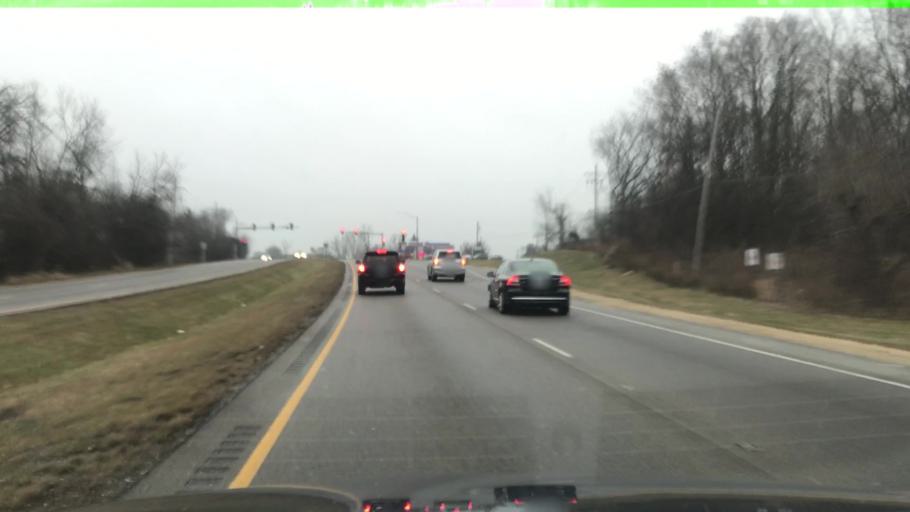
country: US
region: Illinois
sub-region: Lake County
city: Deer Park
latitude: 42.1778
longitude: -88.0763
